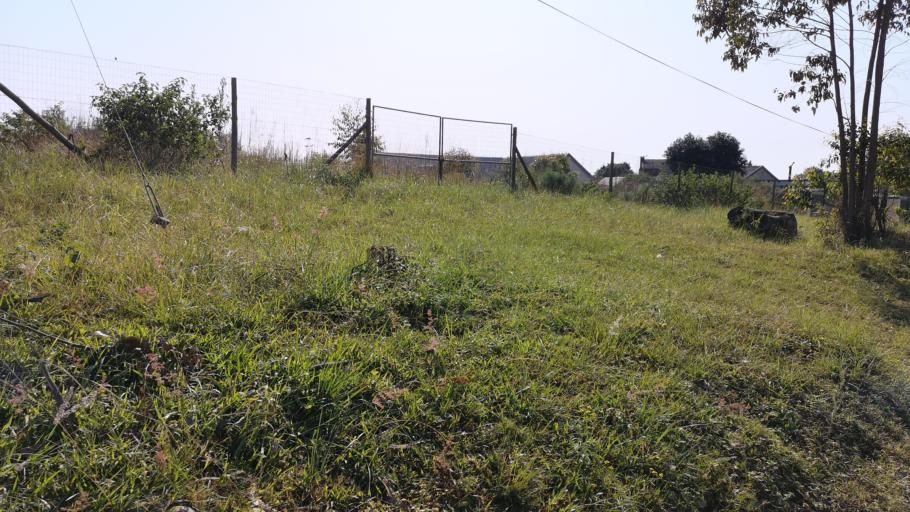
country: ZA
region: KwaZulu-Natal
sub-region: eThekwini Metropolitan Municipality
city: Mpumalanga
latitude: -29.7364
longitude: 30.6844
